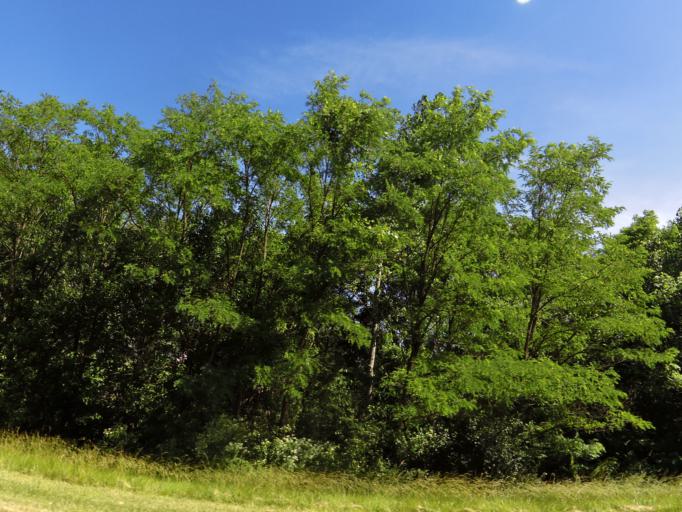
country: US
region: Illinois
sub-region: Vermilion County
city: Danville
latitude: 40.1327
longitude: -87.5708
